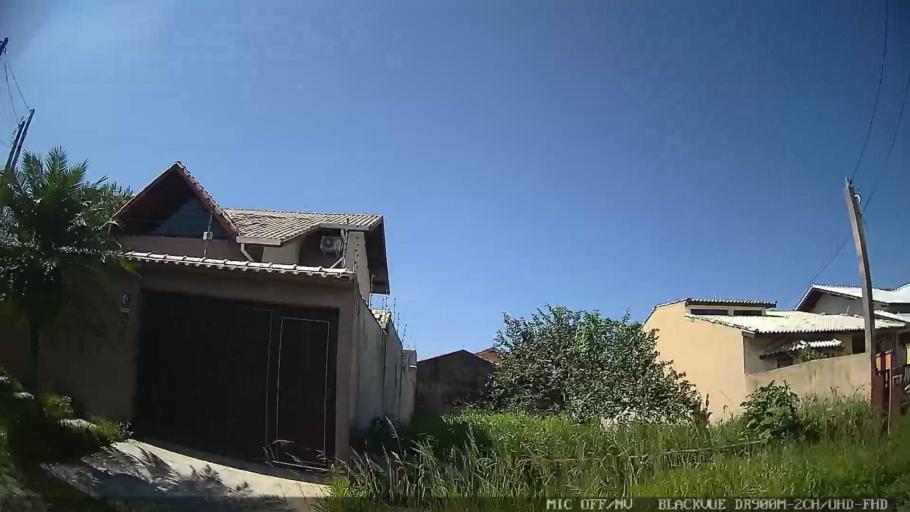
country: BR
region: Sao Paulo
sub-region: Peruibe
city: Peruibe
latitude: -24.2989
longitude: -46.9706
